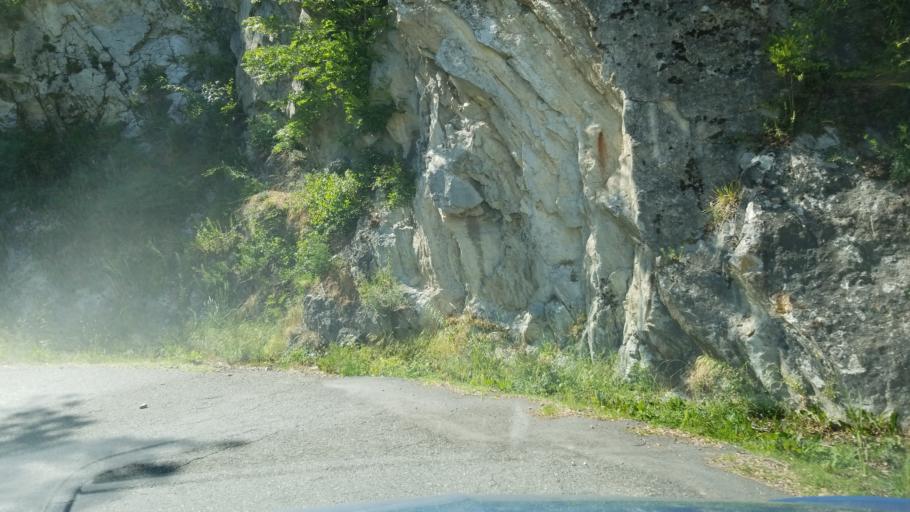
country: FR
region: Rhone-Alpes
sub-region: Departement de la Savoie
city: Saint-Jean-de-Maurienne
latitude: 45.3186
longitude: 6.3371
